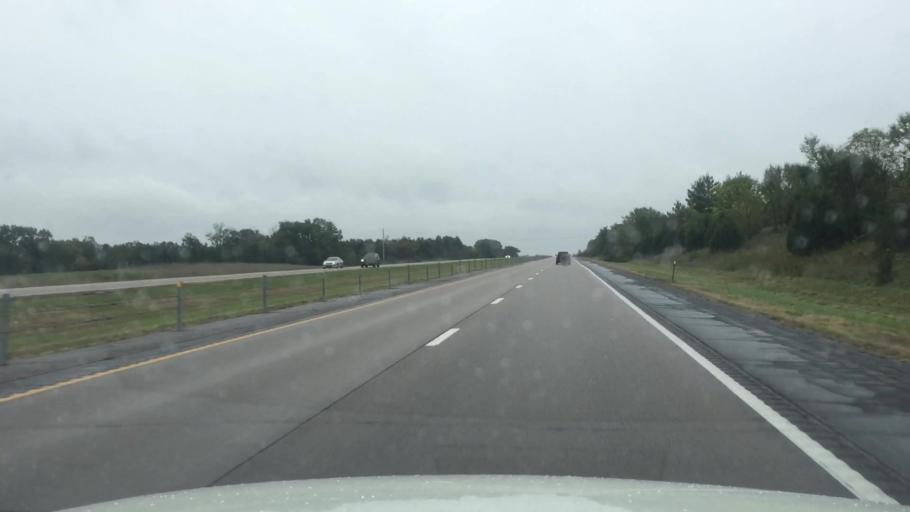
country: US
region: Missouri
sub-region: Boone County
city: Ashland
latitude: 38.7227
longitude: -92.2544
